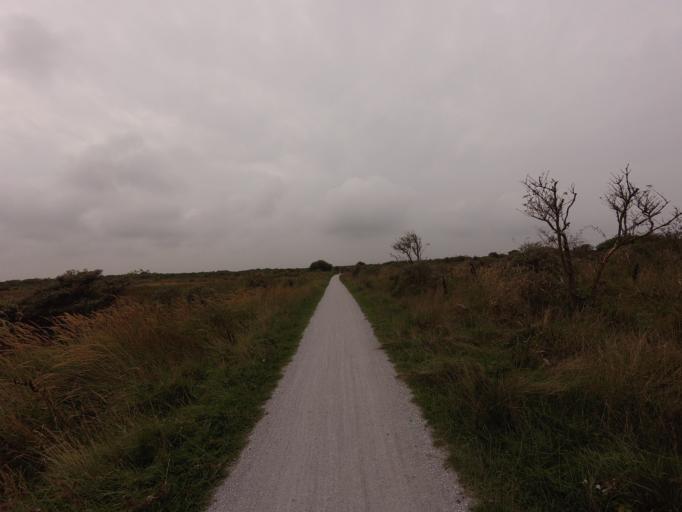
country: NL
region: Friesland
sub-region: Gemeente Schiermonnikoog
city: Schiermonnikoog
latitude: 53.4891
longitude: 6.2045
